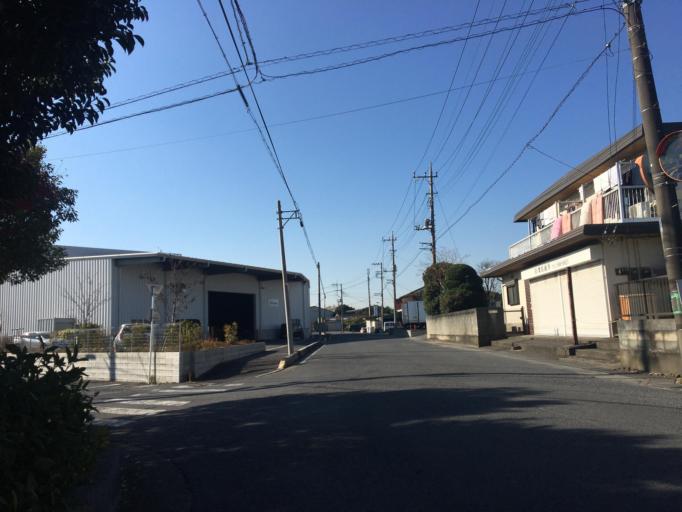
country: JP
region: Saitama
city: Yashio-shi
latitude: 35.8092
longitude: 139.8244
